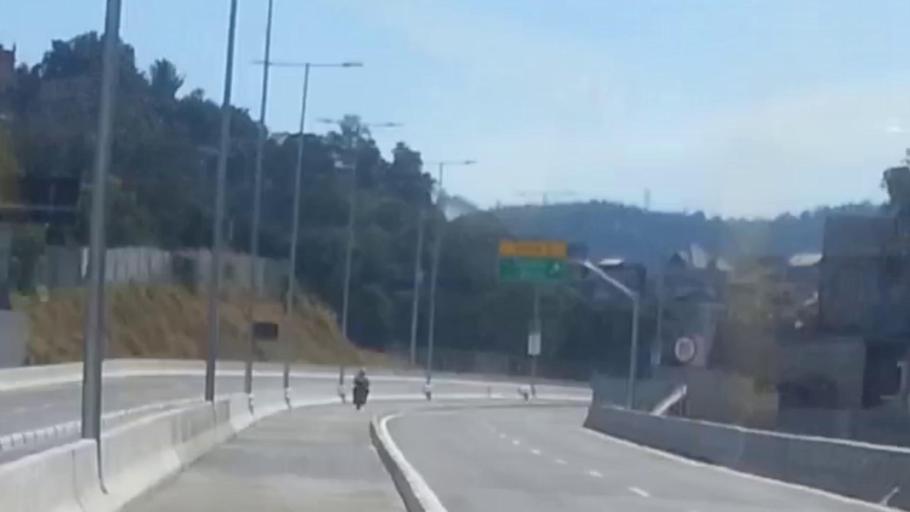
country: BR
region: Rio de Janeiro
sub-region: Nilopolis
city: Nilopolis
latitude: -22.9254
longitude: -43.3971
